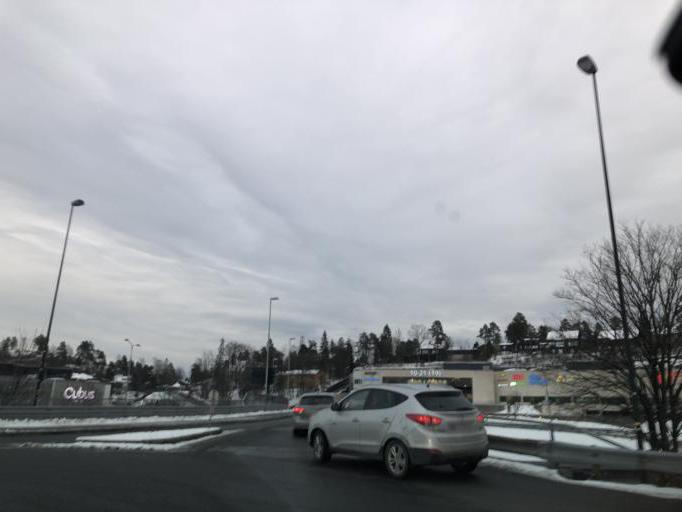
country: NO
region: Akershus
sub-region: Asker
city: Billingstad
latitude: 59.8752
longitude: 10.5010
